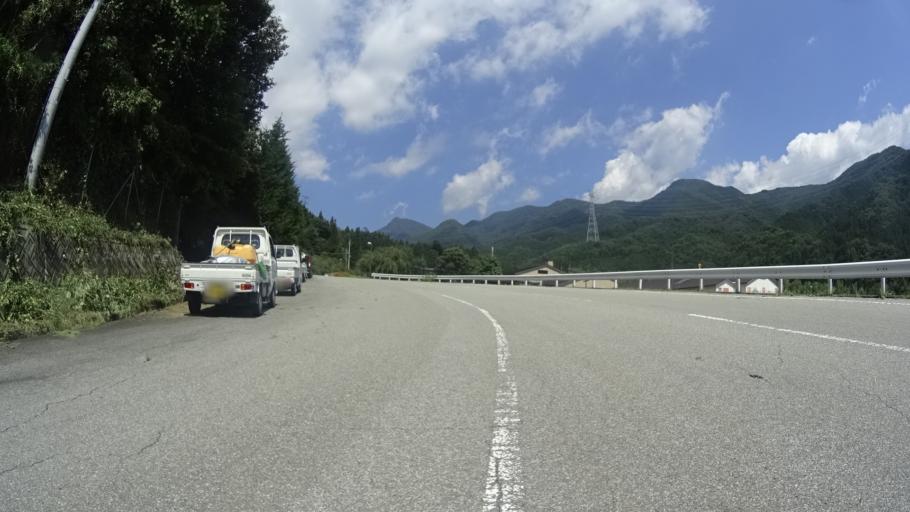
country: JP
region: Yamanashi
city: Enzan
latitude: 35.7739
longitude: 138.6970
